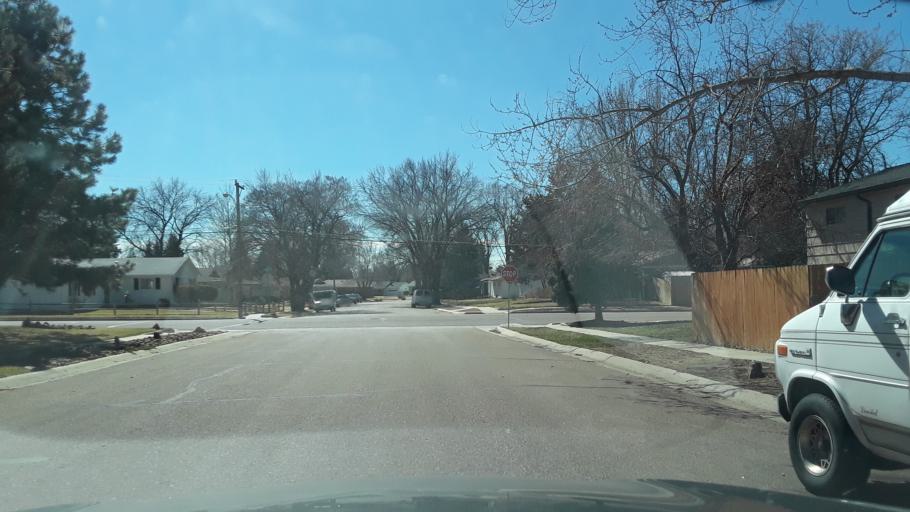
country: US
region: Colorado
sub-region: El Paso County
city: Colorado Springs
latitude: 38.8724
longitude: -104.8068
